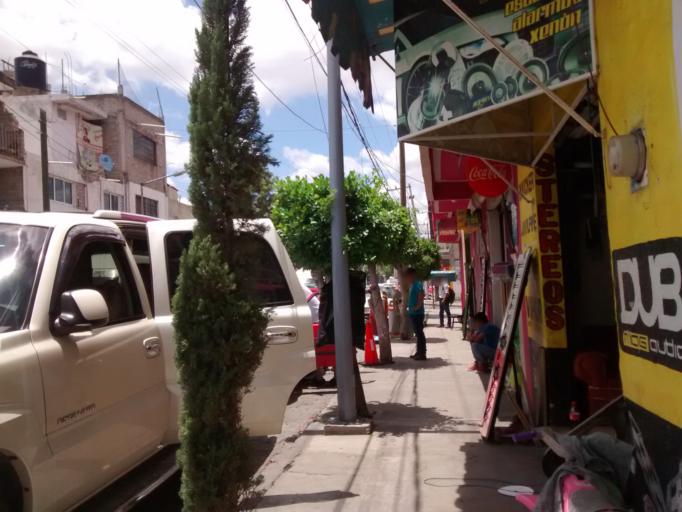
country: MX
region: Puebla
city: Tehuacan
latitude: 18.4564
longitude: -97.3895
